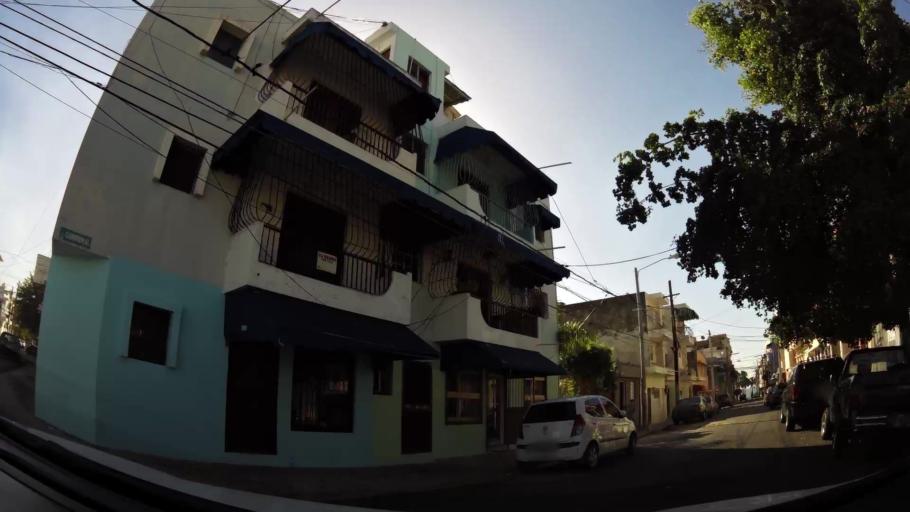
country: DO
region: Nacional
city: Ciudad Nueva
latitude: 18.4684
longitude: -69.8919
